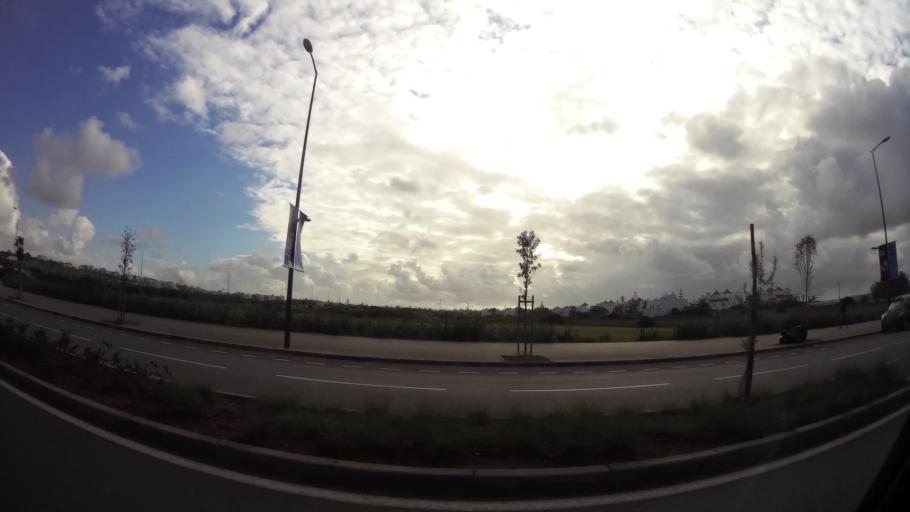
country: MA
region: Grand Casablanca
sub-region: Casablanca
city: Casablanca
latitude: 33.5744
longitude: -7.7008
